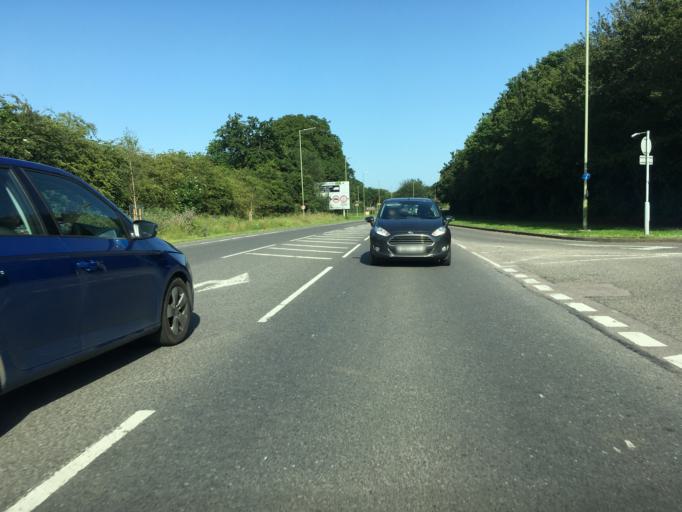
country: GB
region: England
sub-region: Oxfordshire
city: Bicester
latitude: 51.9150
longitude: -1.1471
